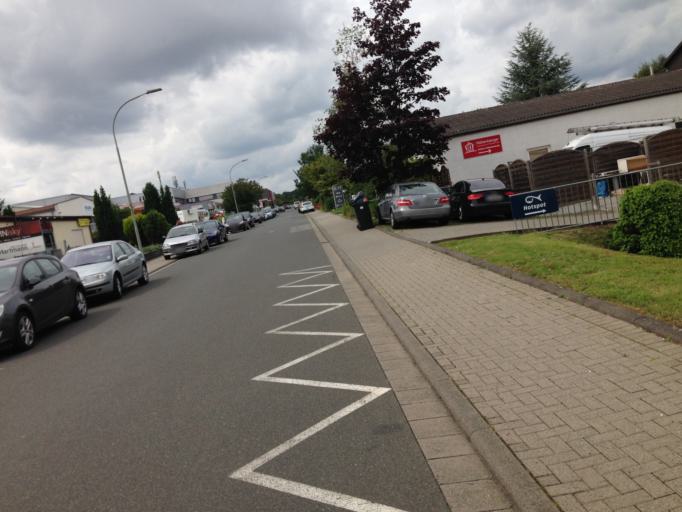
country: DE
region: Hesse
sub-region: Regierungsbezirk Giessen
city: Hoernsheim
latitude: 50.5368
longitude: 8.6560
